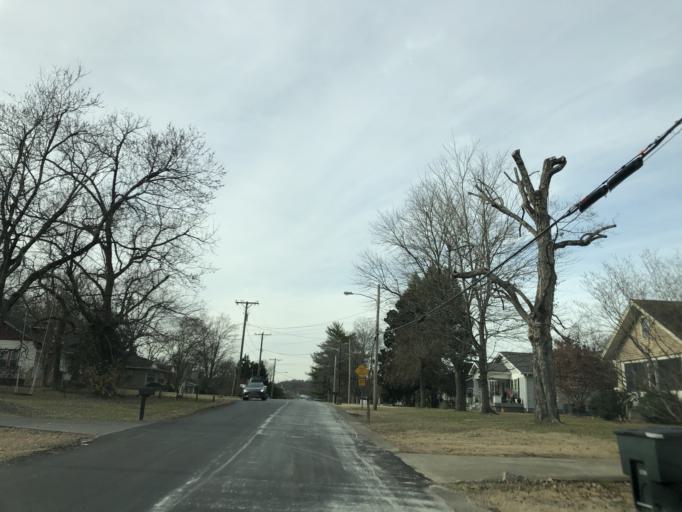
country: US
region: Tennessee
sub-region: Davidson County
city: Nashville
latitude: 36.2126
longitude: -86.7254
